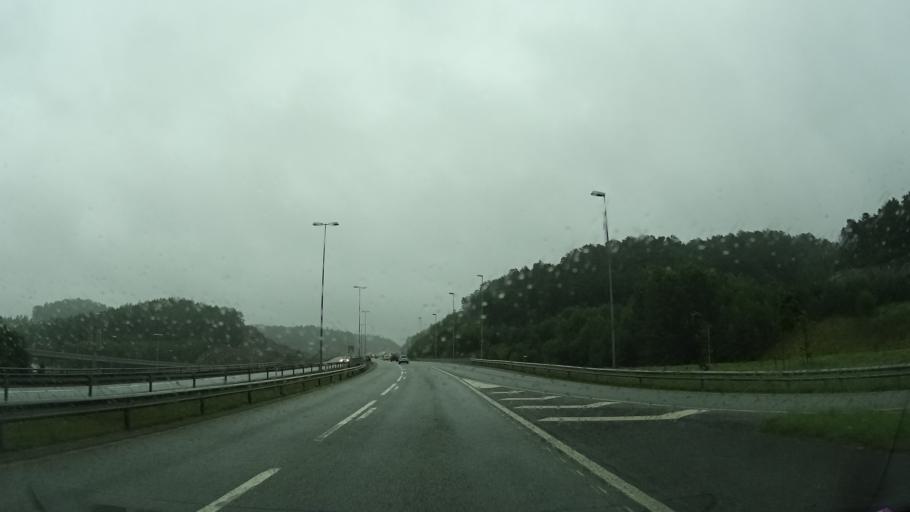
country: NO
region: Vest-Agder
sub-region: Kristiansand
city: Tveit
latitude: 58.1699
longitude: 8.1063
